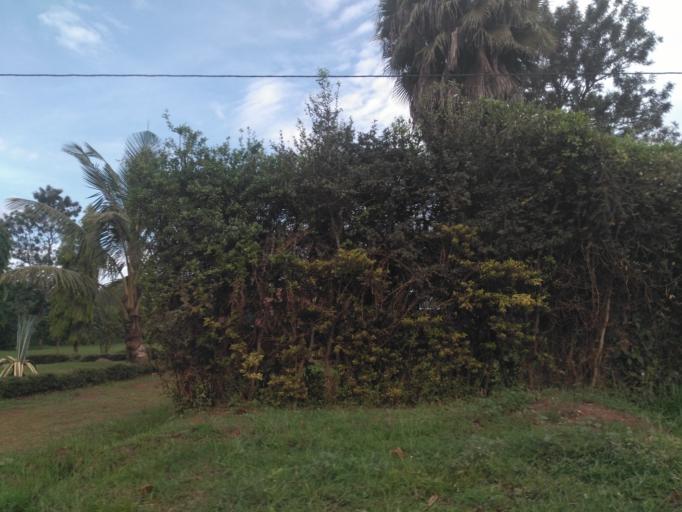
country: UG
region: Central Region
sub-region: Buikwe District
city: Njeru
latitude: 0.4013
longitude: 33.1765
